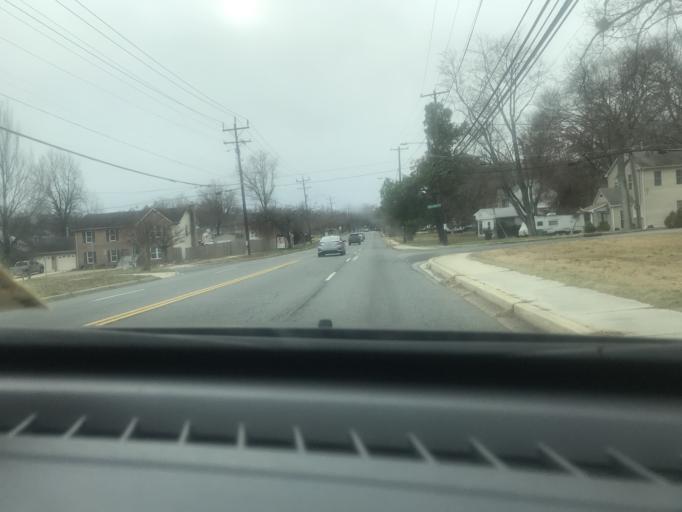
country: US
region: Maryland
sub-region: Prince George's County
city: Temple Hills
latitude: 38.7787
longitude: -76.9494
